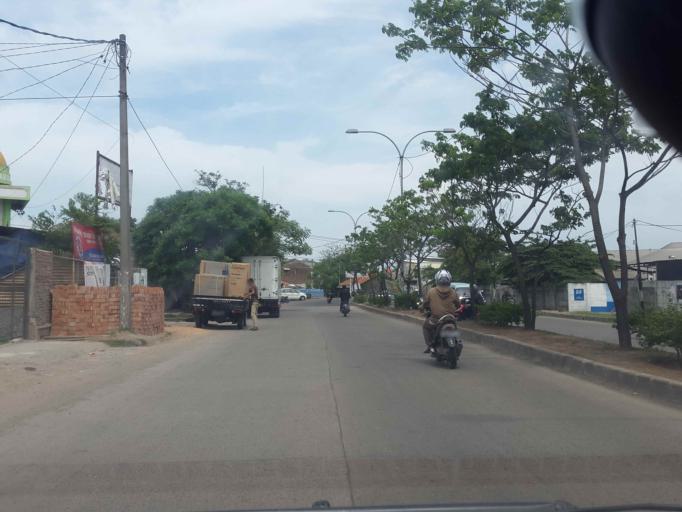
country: ID
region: Banten
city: Tangerang
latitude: -6.1551
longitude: 106.6695
